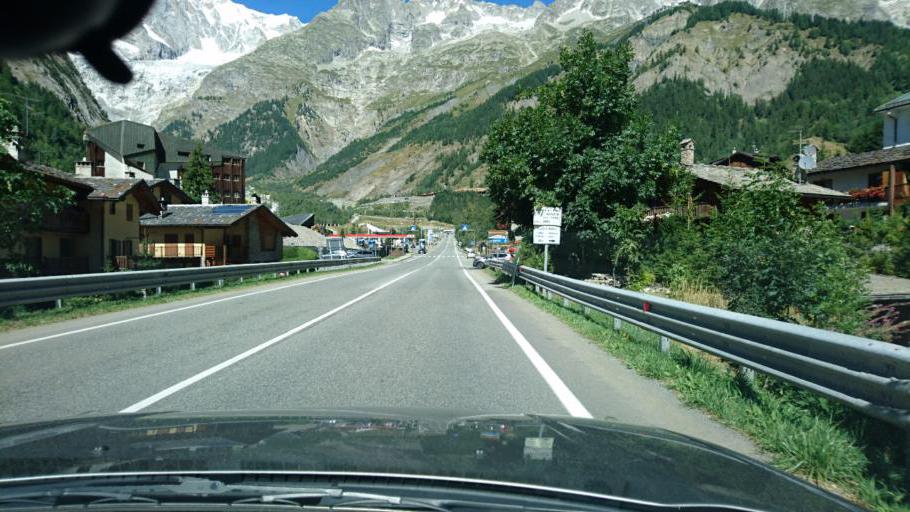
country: IT
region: Aosta Valley
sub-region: Valle d'Aosta
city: Courmayeur
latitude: 45.8109
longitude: 6.9626
